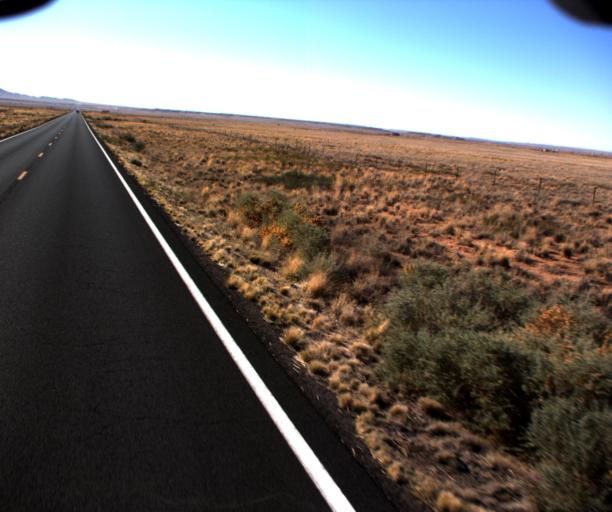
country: US
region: Arizona
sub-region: Navajo County
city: Dilkon
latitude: 35.3788
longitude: -110.4253
